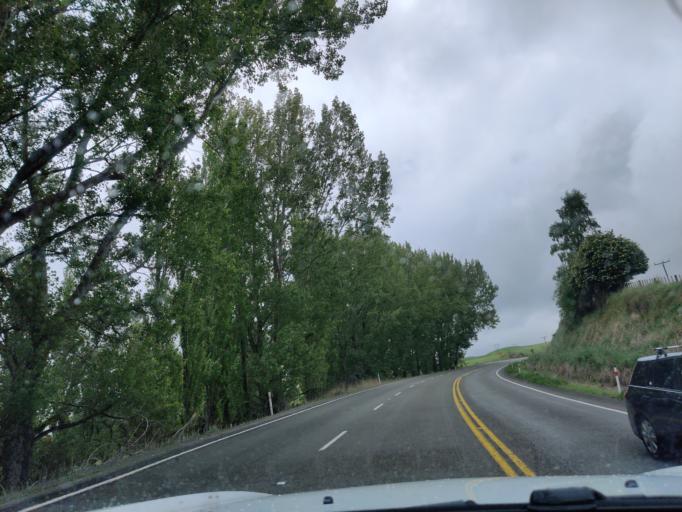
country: NZ
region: Manawatu-Wanganui
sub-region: Ruapehu District
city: Waiouru
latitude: -39.5359
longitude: 175.6800
